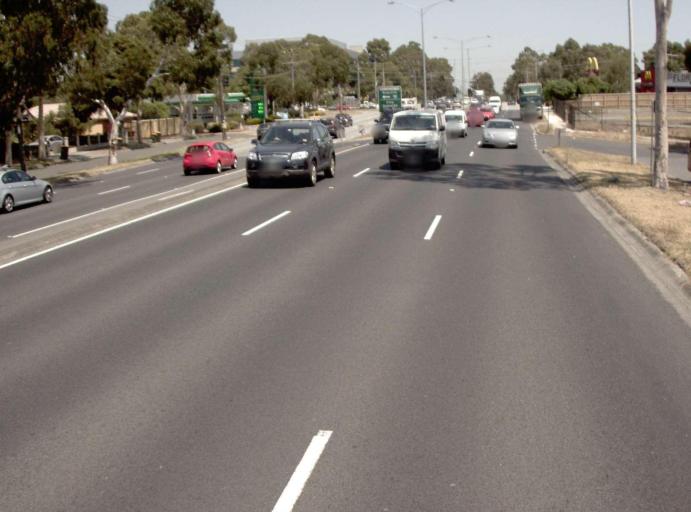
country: AU
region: Victoria
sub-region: Monash
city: Notting Hill
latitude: -37.9167
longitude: 145.1589
